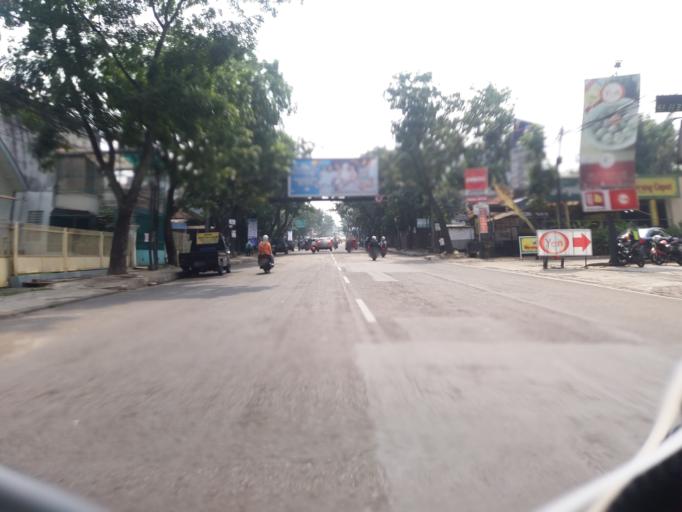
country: ID
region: West Java
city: Bandung
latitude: -6.9087
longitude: 107.5977
